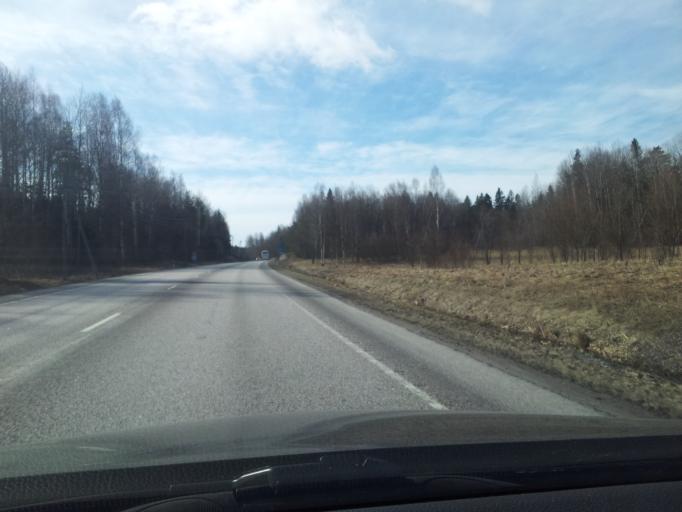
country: FI
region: Uusimaa
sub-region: Helsinki
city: Kirkkonummi
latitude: 60.1471
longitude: 24.5405
